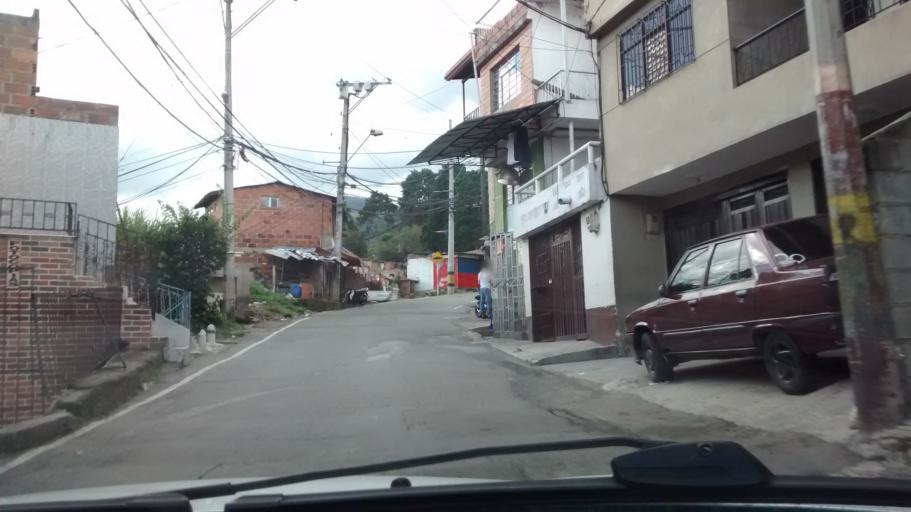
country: CO
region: Antioquia
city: Medellin
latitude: 6.2736
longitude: -75.6283
